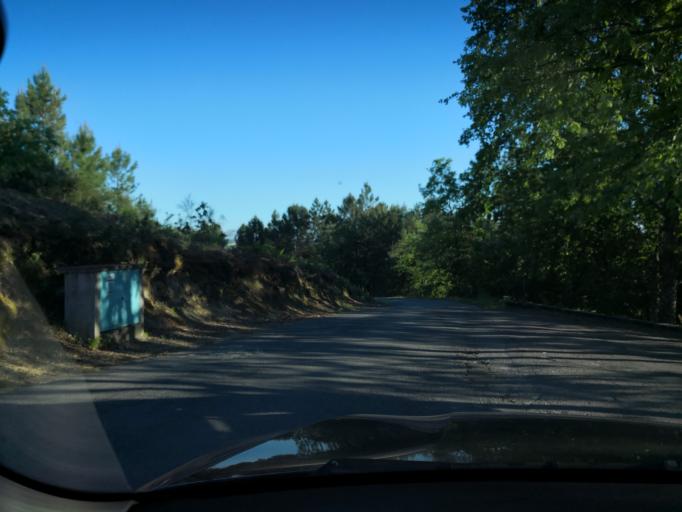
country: PT
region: Vila Real
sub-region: Vila Real
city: Vila Real
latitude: 41.3388
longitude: -7.7369
